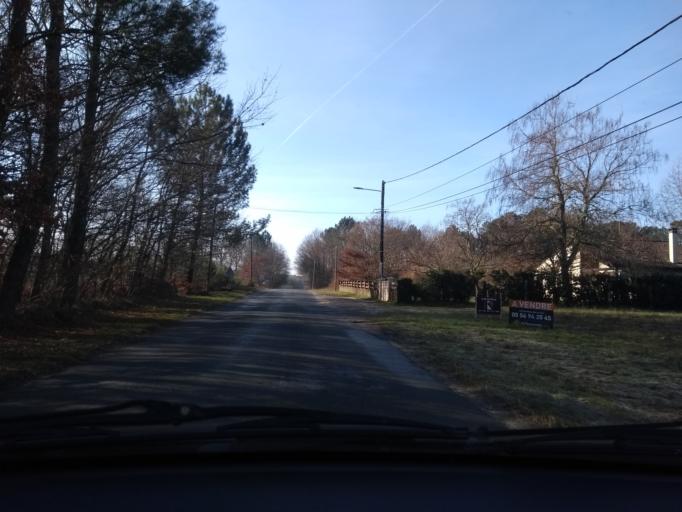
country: FR
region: Aquitaine
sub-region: Departement de la Gironde
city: Salles
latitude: 44.5824
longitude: -0.8561
